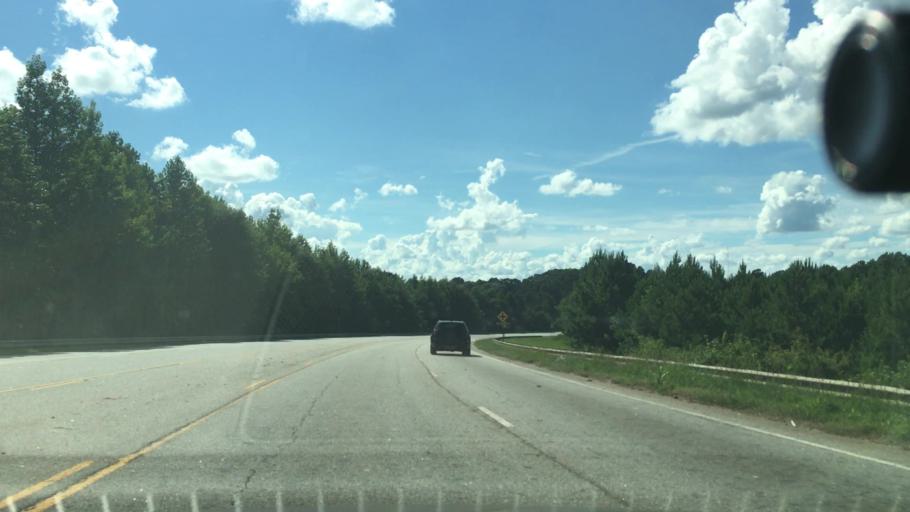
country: US
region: Georgia
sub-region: Spalding County
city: East Griffin
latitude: 33.2328
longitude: -84.2375
